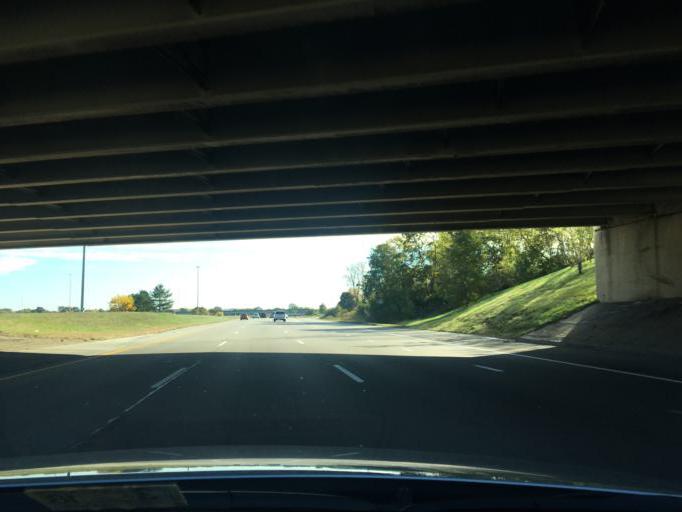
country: US
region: Michigan
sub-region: Wayne County
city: Plymouth
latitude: 42.3867
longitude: -83.4444
